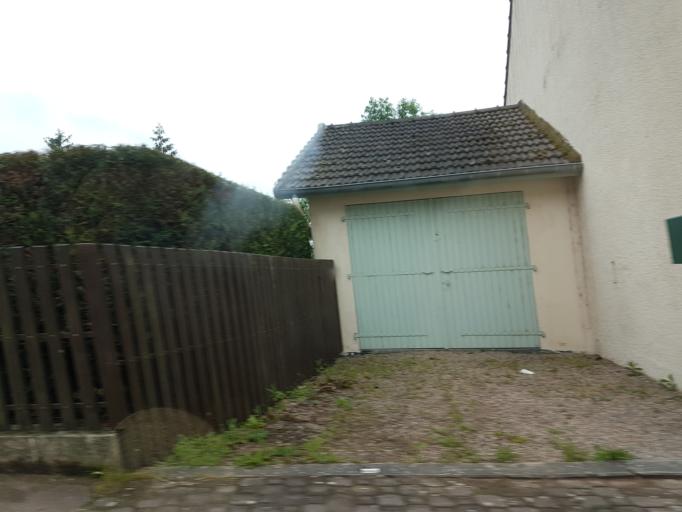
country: FR
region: Bourgogne
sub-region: Departement de la Nievre
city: Corbigny
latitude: 47.2620
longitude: 3.6800
